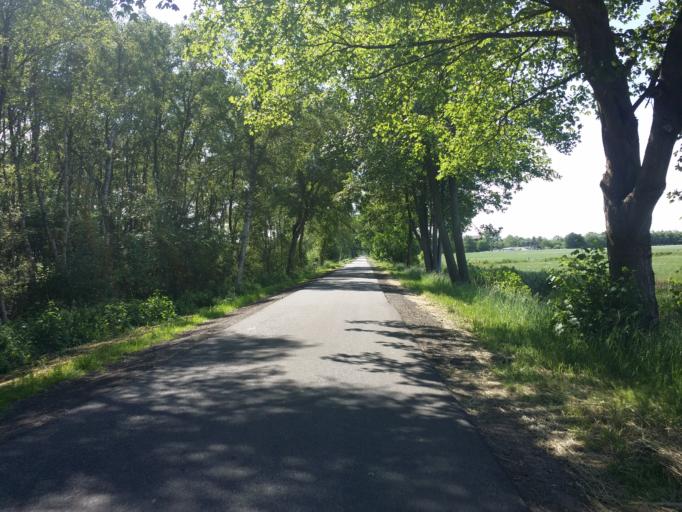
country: DE
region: Lower Saxony
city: Oldenburg
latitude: 53.2059
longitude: 8.3197
